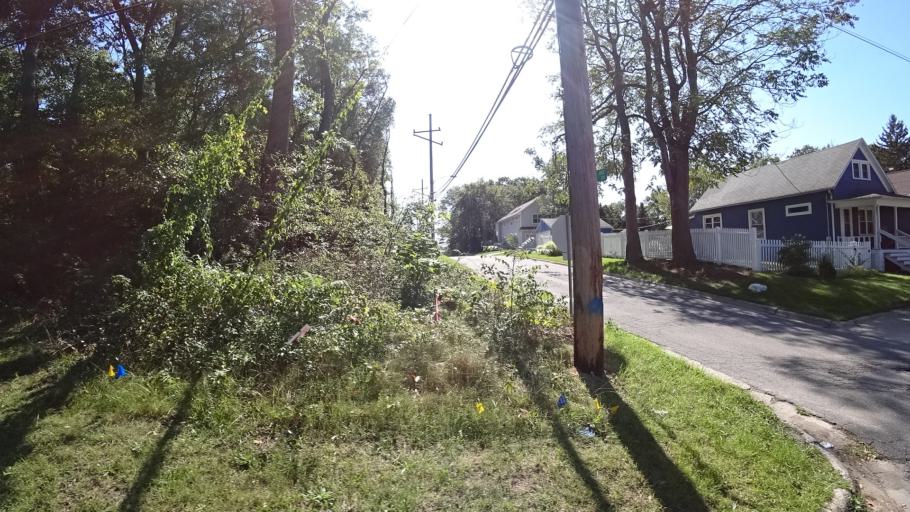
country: US
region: Indiana
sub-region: LaPorte County
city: Michigan City
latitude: 41.7256
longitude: -86.8908
